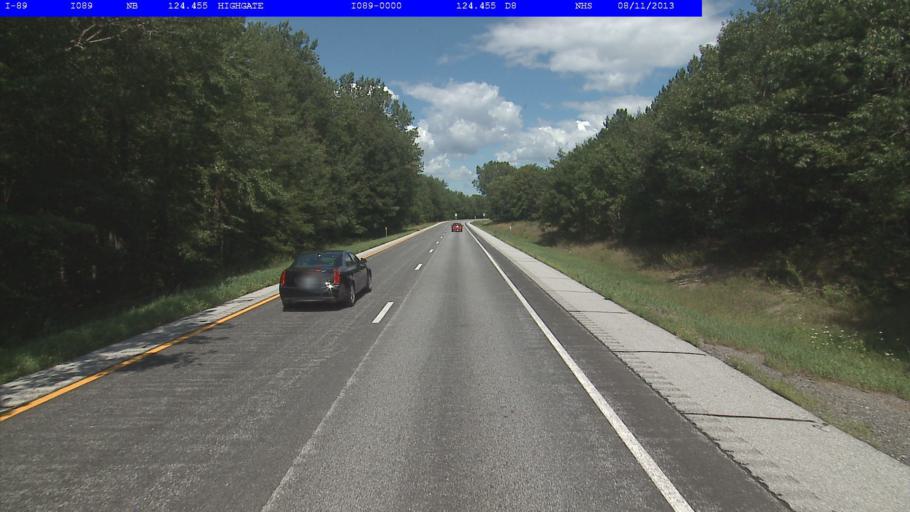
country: US
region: Vermont
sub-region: Franklin County
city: Swanton
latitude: 44.9374
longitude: -73.1136
